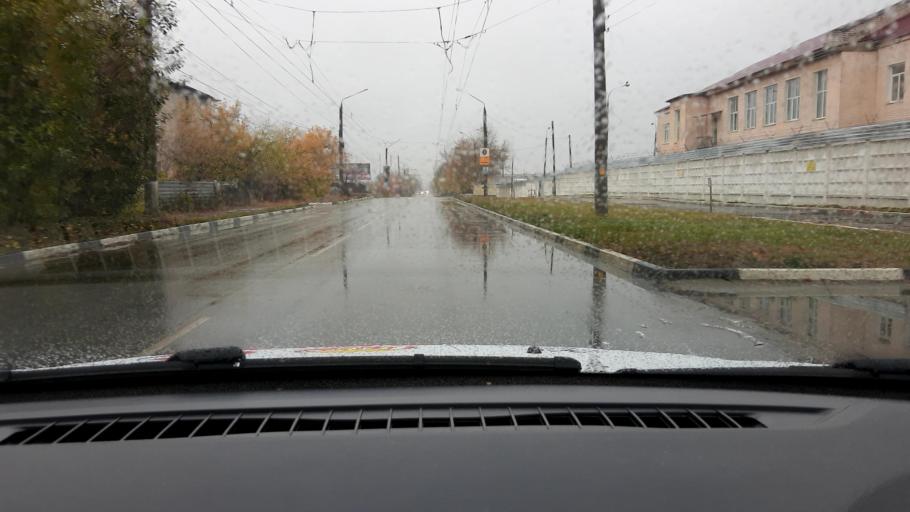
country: RU
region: Nizjnij Novgorod
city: Dzerzhinsk
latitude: 56.2457
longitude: 43.4803
